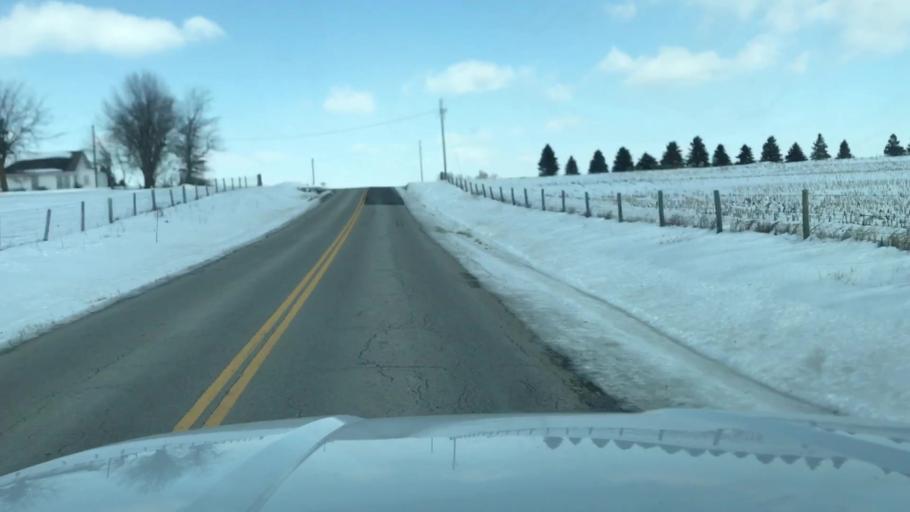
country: US
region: Missouri
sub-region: Nodaway County
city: Maryville
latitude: 40.3613
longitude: -94.7219
